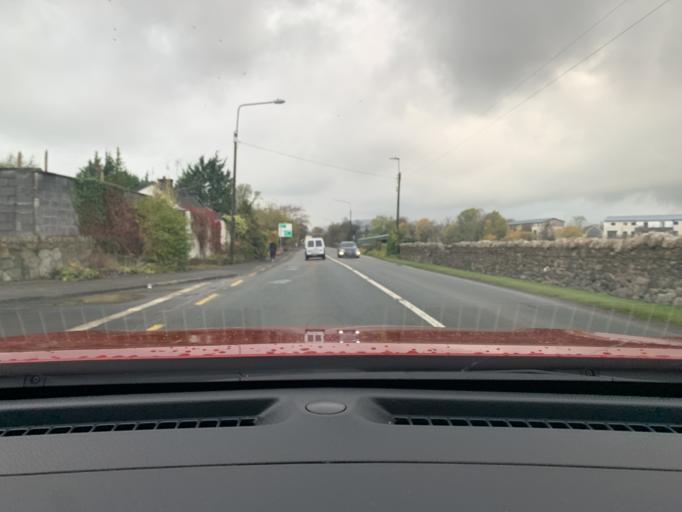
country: IE
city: Ballisodare
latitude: 54.2070
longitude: -8.5060
